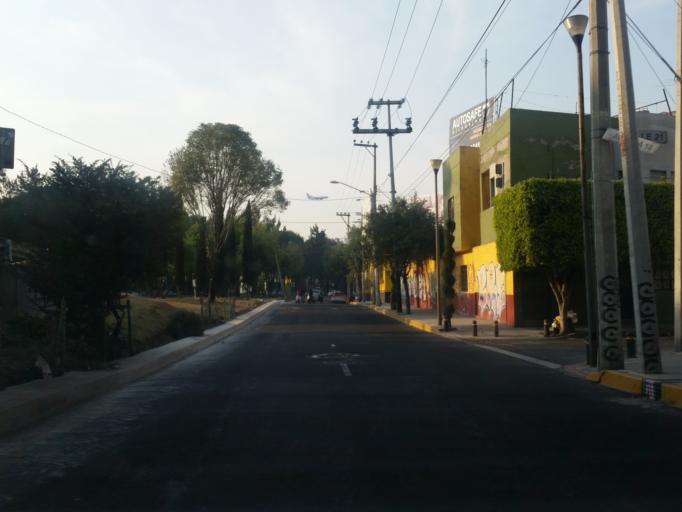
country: MX
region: Mexico City
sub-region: Iztacalco
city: Iztacalco
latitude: 19.4099
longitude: -99.0965
